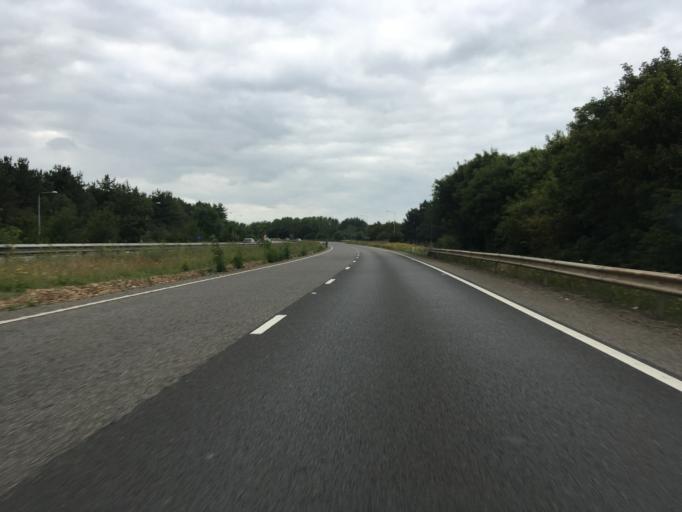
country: GB
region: England
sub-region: Milton Keynes
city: Simpson
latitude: 52.0096
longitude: -0.7127
